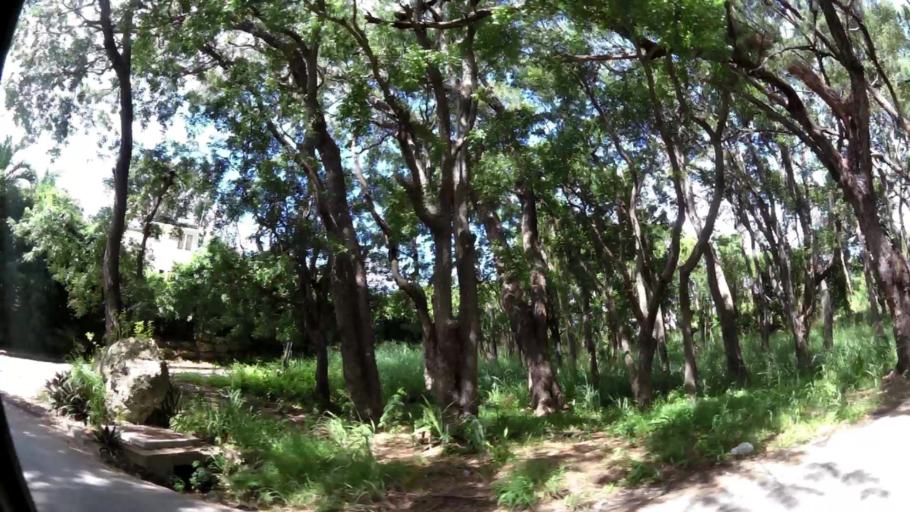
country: BB
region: Saint James
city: Holetown
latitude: 13.2049
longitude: -59.6331
